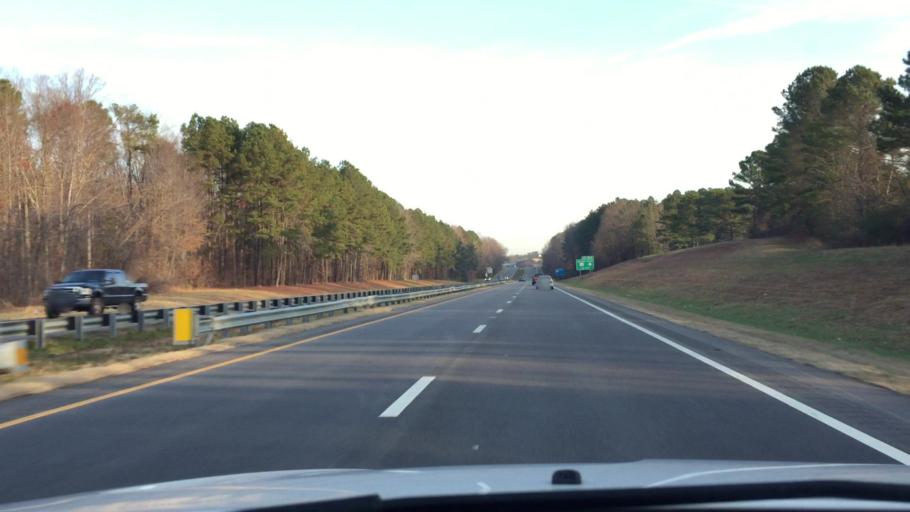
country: US
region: North Carolina
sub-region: Lee County
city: Sanford
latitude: 35.4736
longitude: -79.2012
